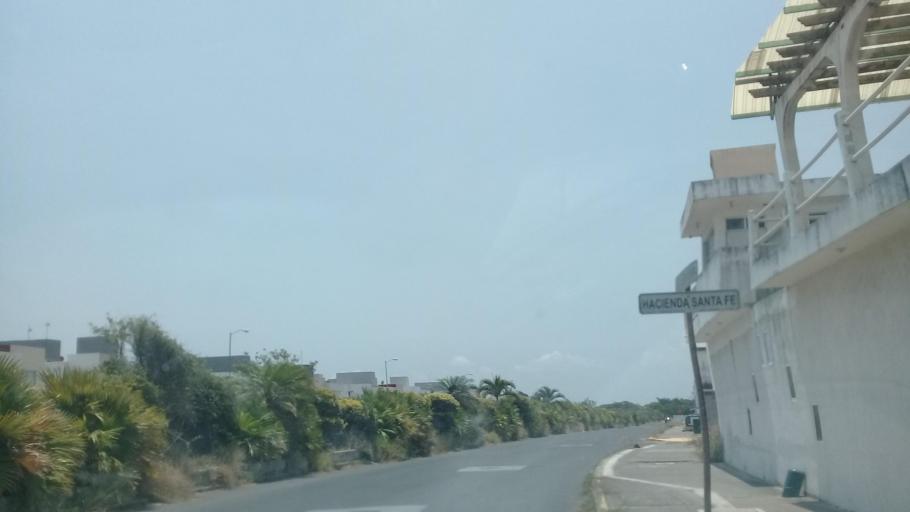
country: MX
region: Veracruz
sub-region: Veracruz
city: Hacienda Sotavento
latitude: 19.1322
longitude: -96.1738
